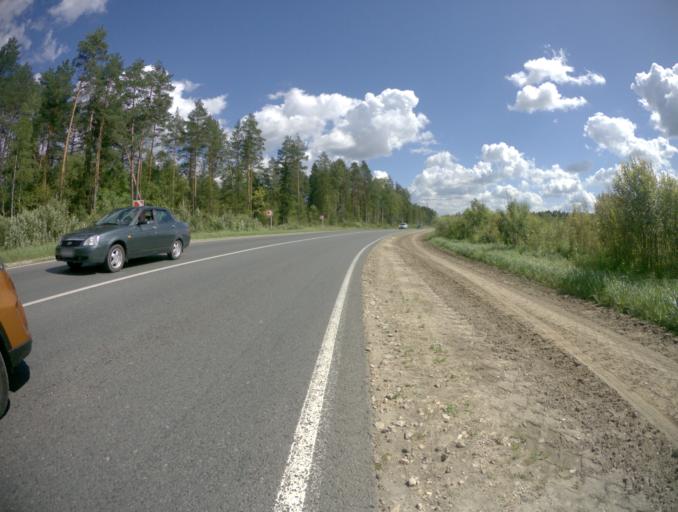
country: RU
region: Vladimir
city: Orgtrud
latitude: 56.0118
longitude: 40.6000
